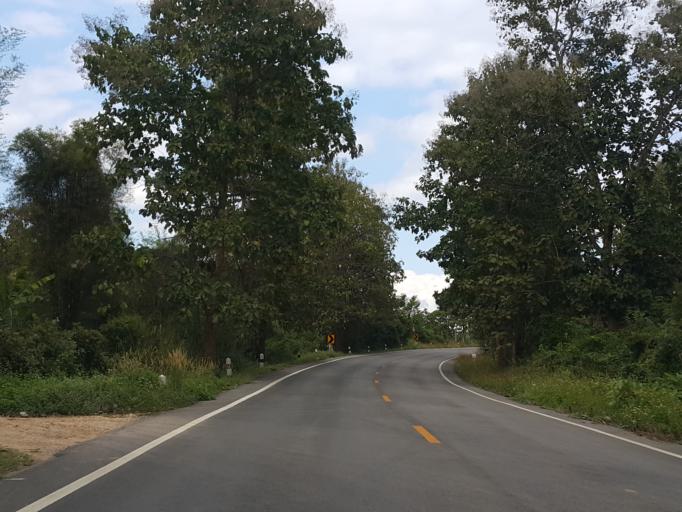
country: TH
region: Lampang
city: Chae Hom
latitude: 18.6156
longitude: 99.4815
